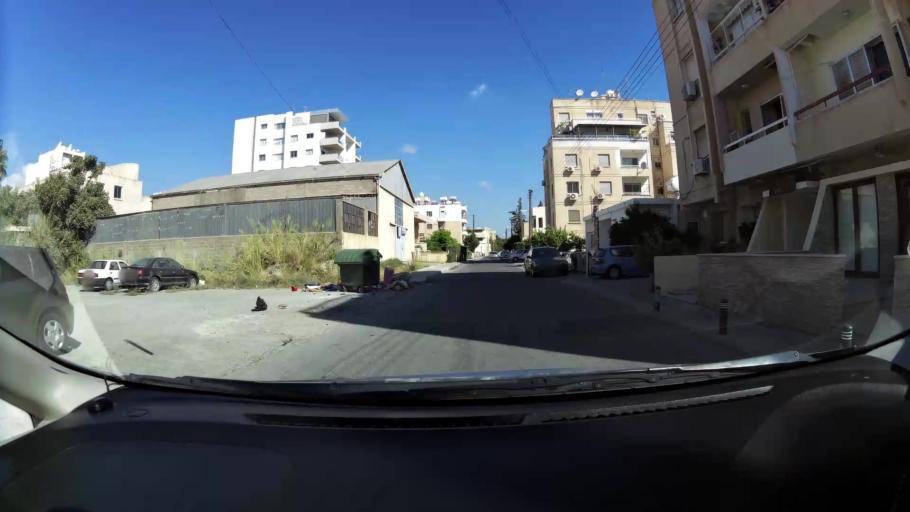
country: CY
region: Larnaka
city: Larnaca
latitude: 34.9235
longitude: 33.6375
